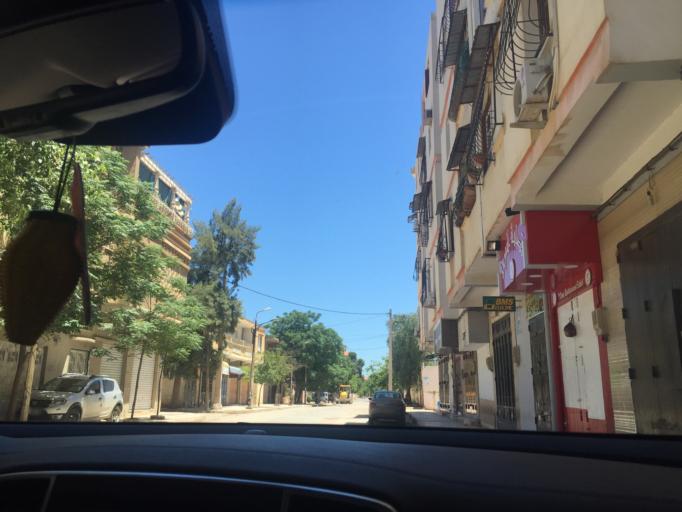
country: DZ
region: Ain Defla
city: Khemis Miliana
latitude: 36.2577
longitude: 2.2162
